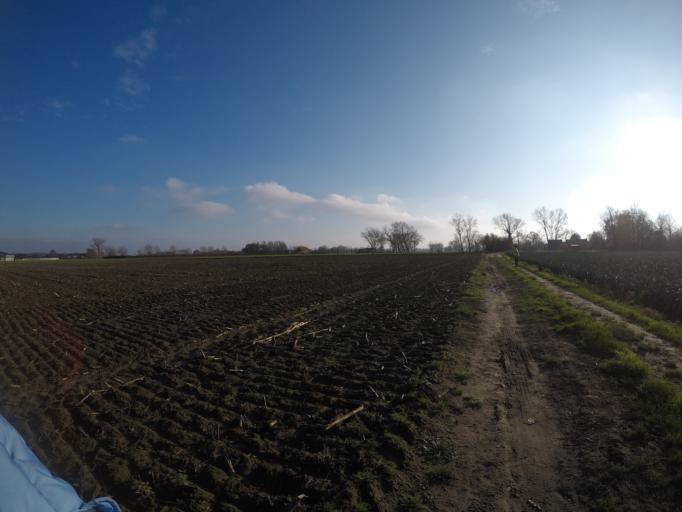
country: BE
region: Flanders
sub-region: Provincie West-Vlaanderen
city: Lichtervelde
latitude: 51.0603
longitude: 3.1939
